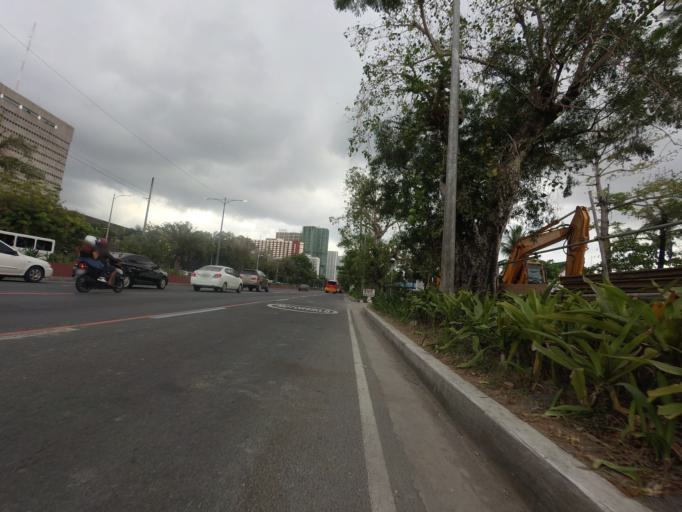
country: PH
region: Metro Manila
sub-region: City of Manila
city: Port Area
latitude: 14.5629
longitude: 120.9855
